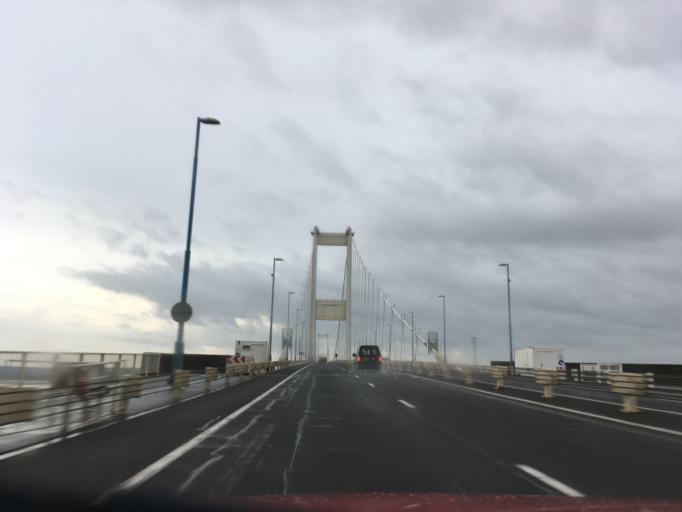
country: GB
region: Wales
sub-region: Monmouthshire
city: Chepstow
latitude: 51.6140
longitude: -2.6510
